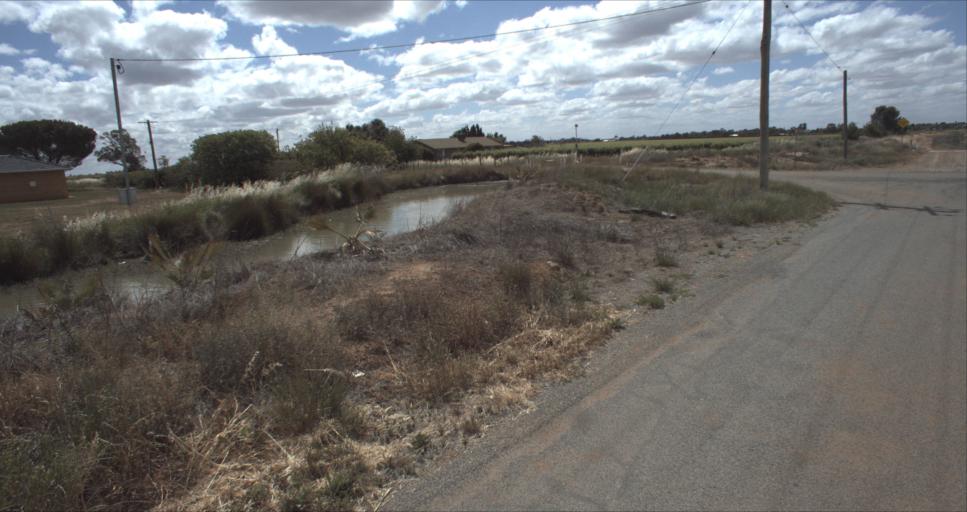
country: AU
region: New South Wales
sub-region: Leeton
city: Leeton
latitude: -34.5805
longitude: 146.3923
